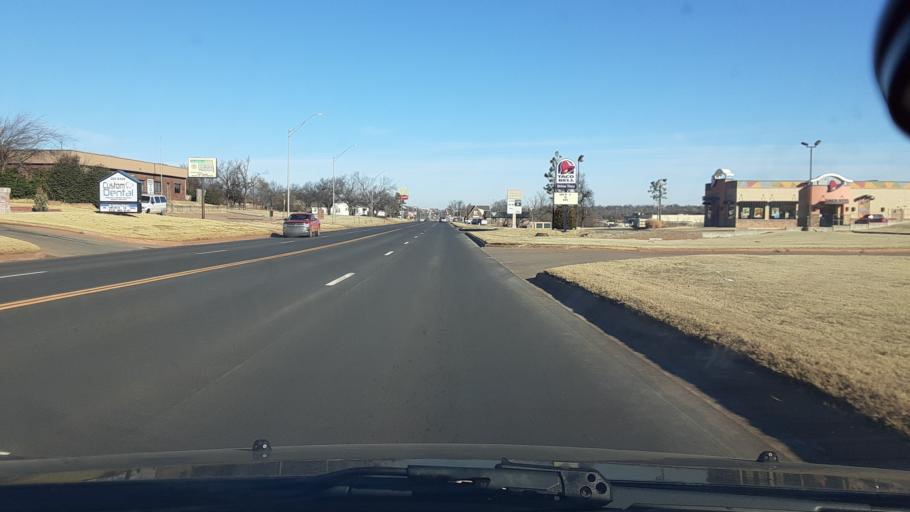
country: US
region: Oklahoma
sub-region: Logan County
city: Guthrie
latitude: 35.8578
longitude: -97.4254
